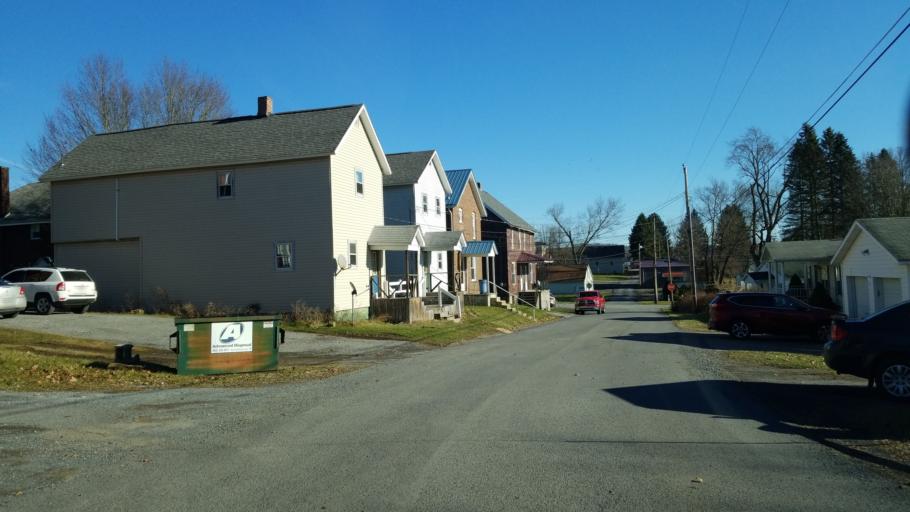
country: US
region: Pennsylvania
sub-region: Jefferson County
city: Falls Creek
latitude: 41.1442
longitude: -78.8011
